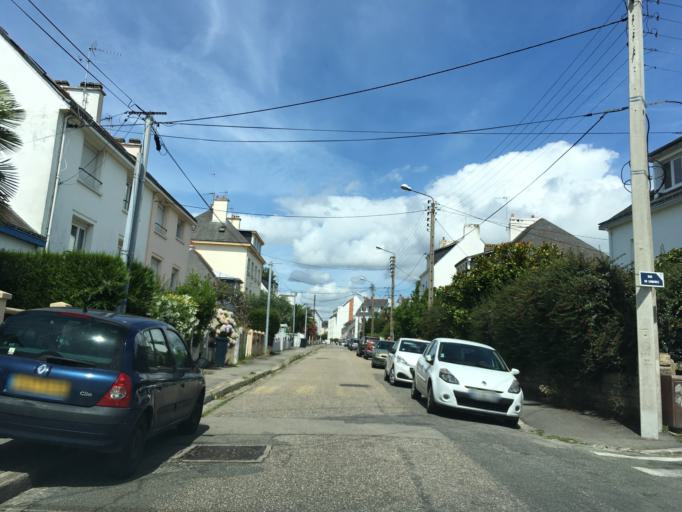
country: FR
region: Brittany
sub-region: Departement du Morbihan
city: Lorient
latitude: 47.7374
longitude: -3.3724
